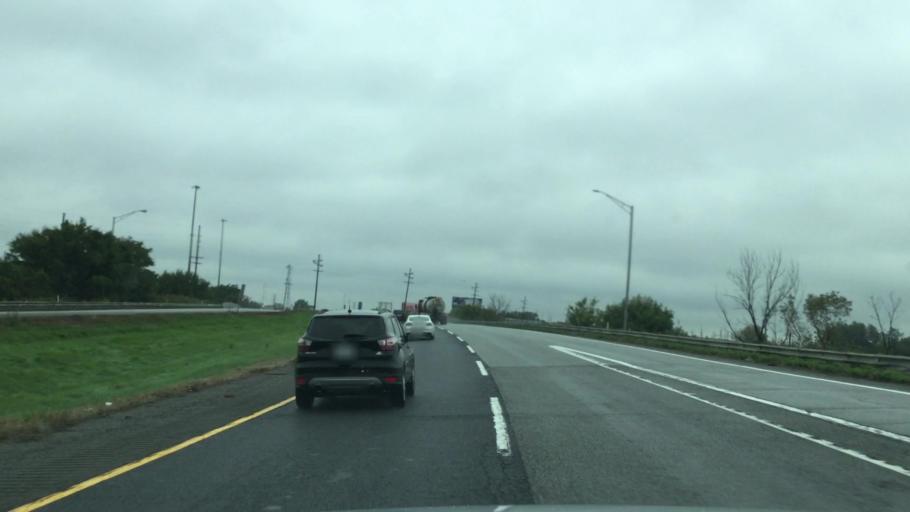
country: US
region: Illinois
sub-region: Cook County
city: Calumet City
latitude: 41.6430
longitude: -87.5069
